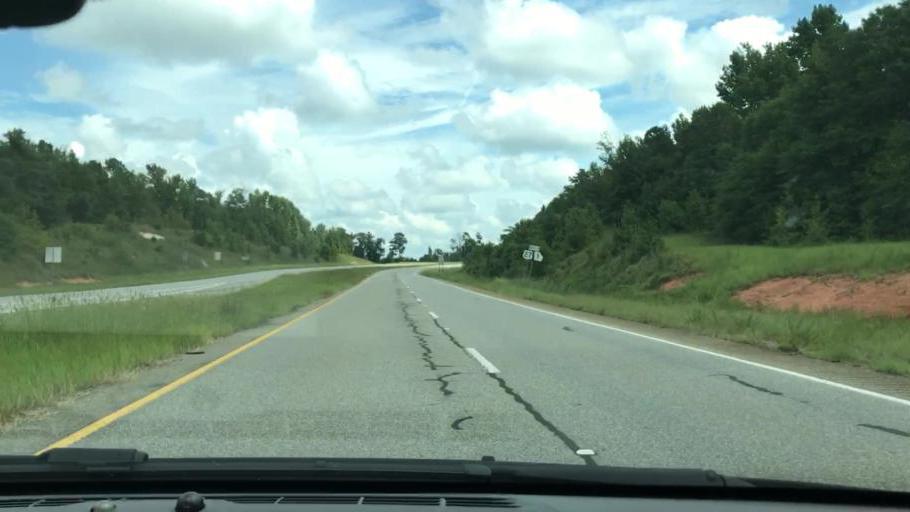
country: US
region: Georgia
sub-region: Stewart County
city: Lumpkin
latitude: 32.0553
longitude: -84.8061
